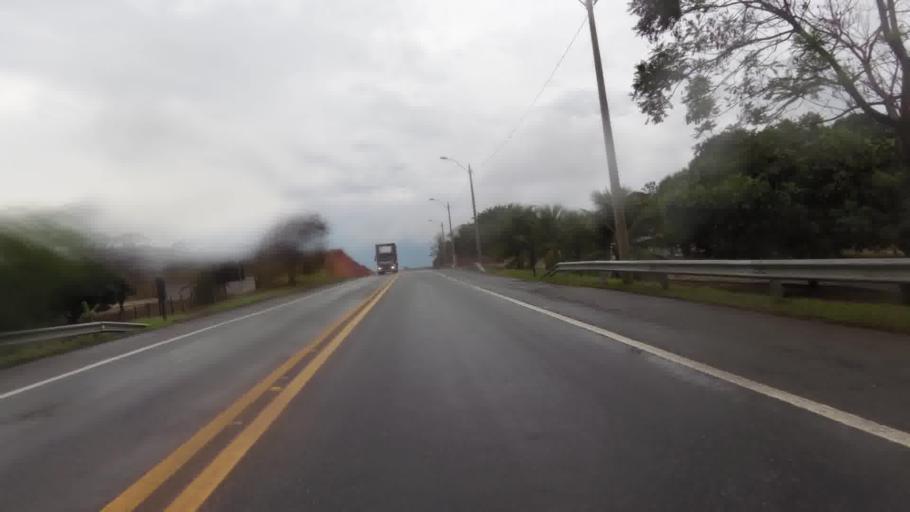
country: BR
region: Rio de Janeiro
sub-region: Campos Dos Goytacazes
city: Campos
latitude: -21.5018
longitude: -41.3394
